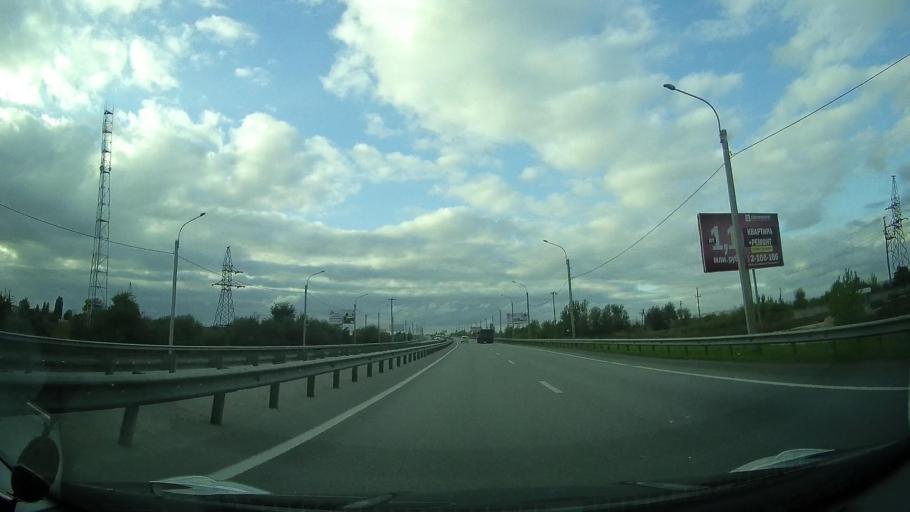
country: RU
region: Rostov
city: Bataysk
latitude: 47.1574
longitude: 39.7676
